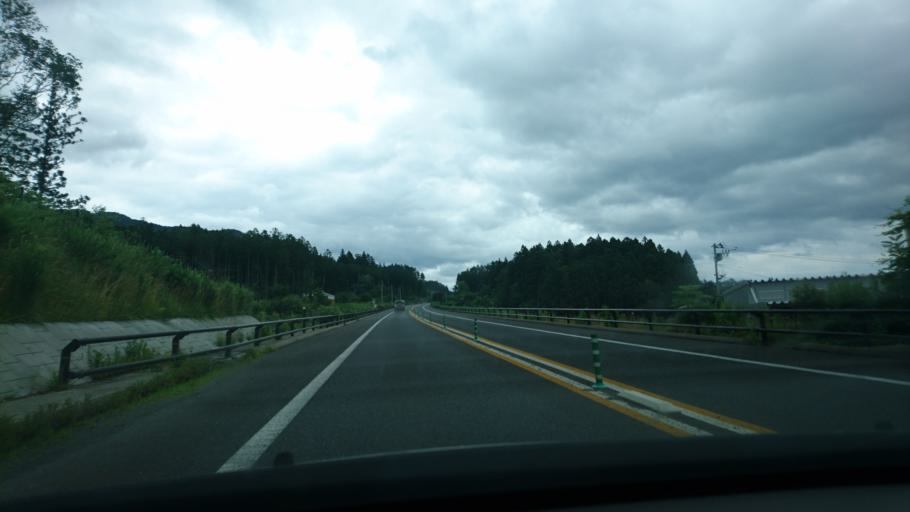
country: JP
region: Iwate
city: Ofunato
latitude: 39.0316
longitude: 141.6368
